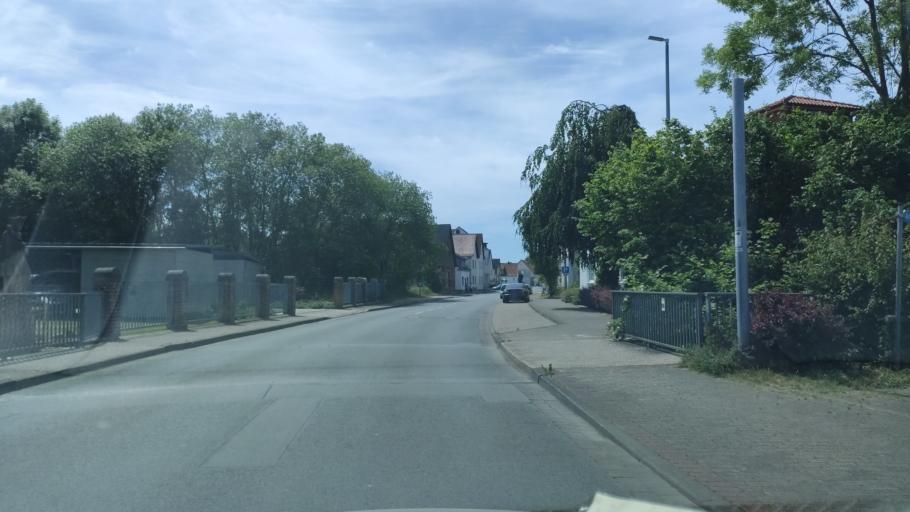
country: DE
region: North Rhine-Westphalia
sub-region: Regierungsbezirk Detmold
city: Steinheim
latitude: 51.8637
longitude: 9.0931
